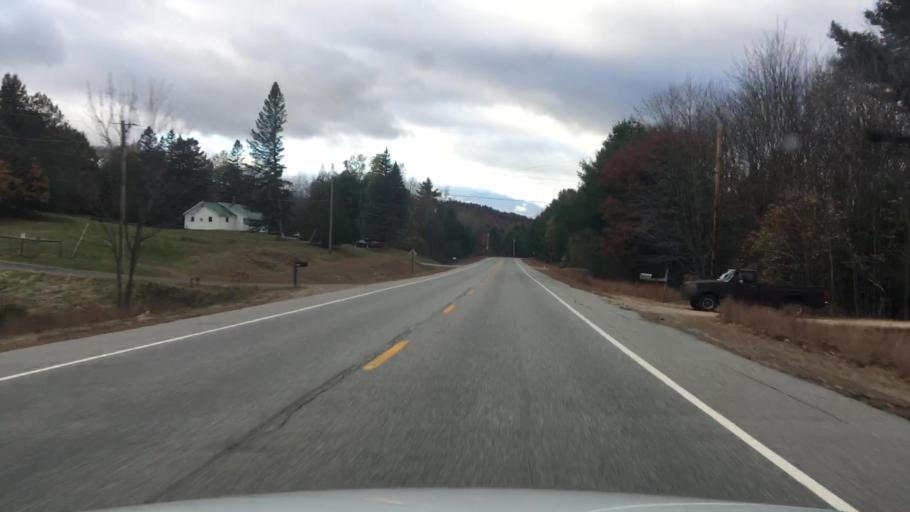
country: US
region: Maine
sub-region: Oxford County
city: Canton
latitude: 44.4186
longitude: -70.2893
